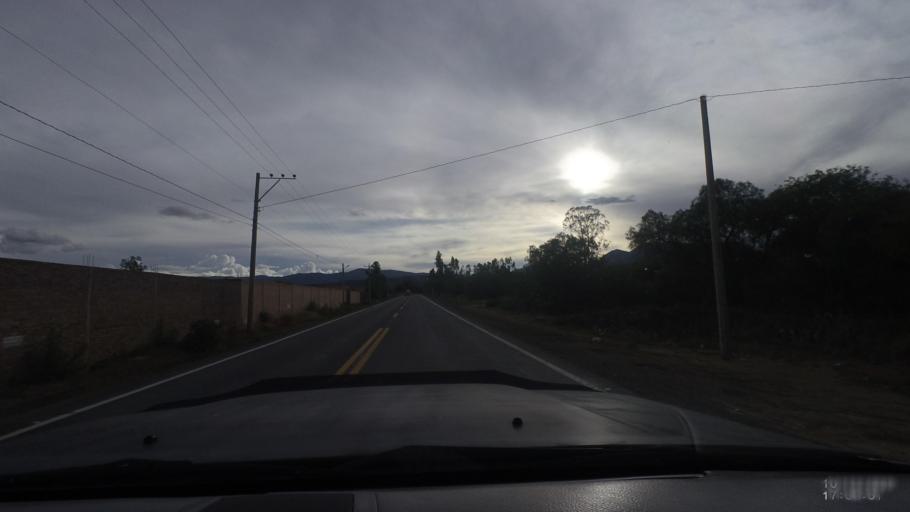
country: BO
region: Cochabamba
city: Tarata
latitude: -17.5812
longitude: -66.0166
